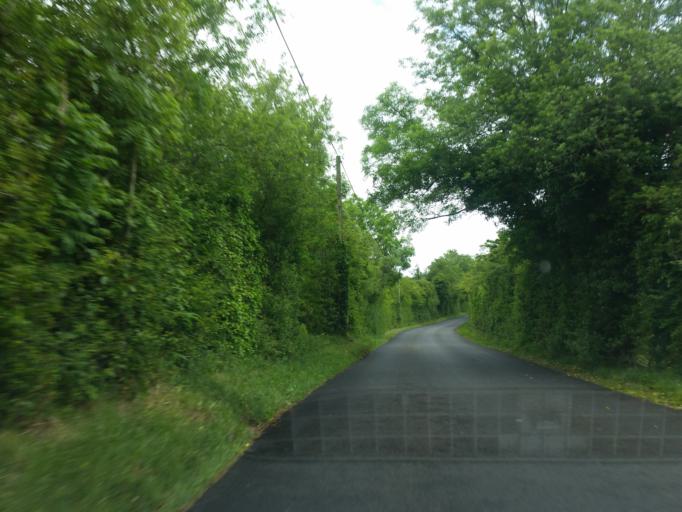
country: GB
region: Northern Ireland
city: Lisnaskea
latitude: 54.2367
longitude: -7.3672
